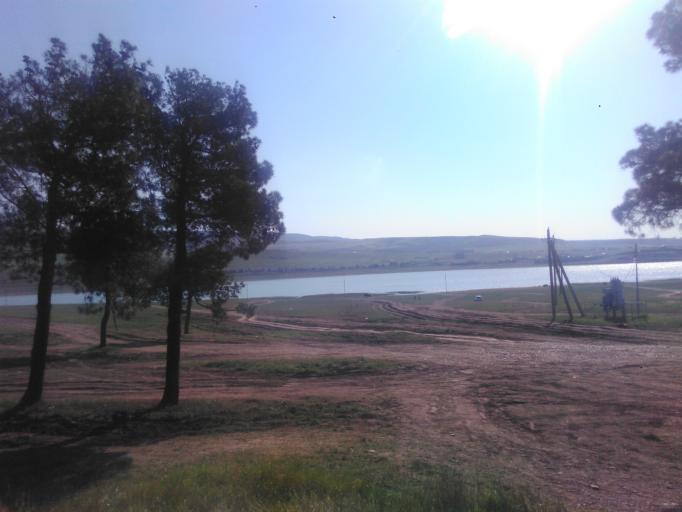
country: GE
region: T'bilisi
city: Tbilisi
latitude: 41.7181
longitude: 44.8768
